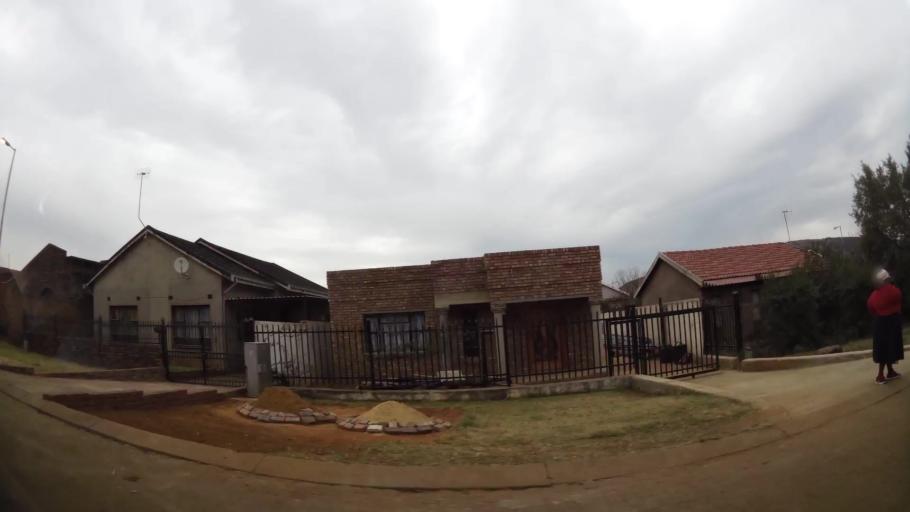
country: ZA
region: Gauteng
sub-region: City of Tshwane Metropolitan Municipality
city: Cullinan
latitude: -25.7059
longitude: 28.3634
